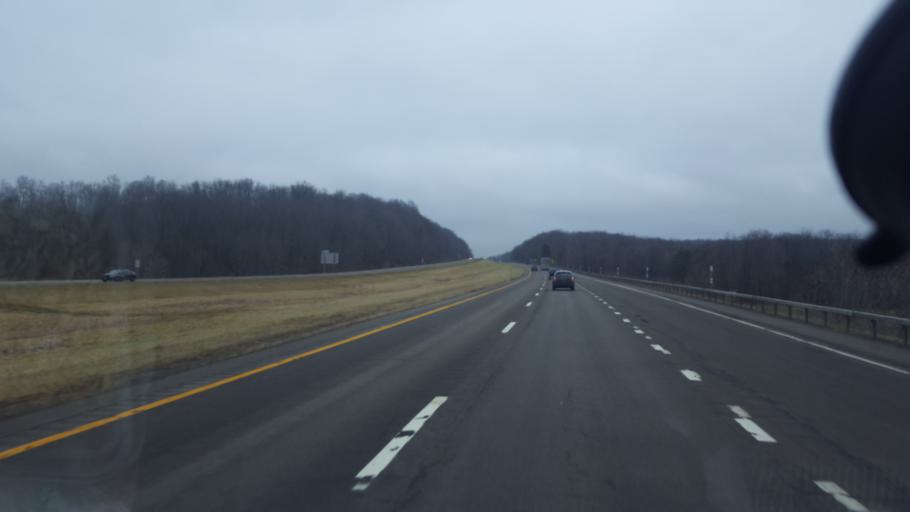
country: US
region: New York
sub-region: Cattaraugus County
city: Randolph
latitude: 42.1439
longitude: -79.0865
